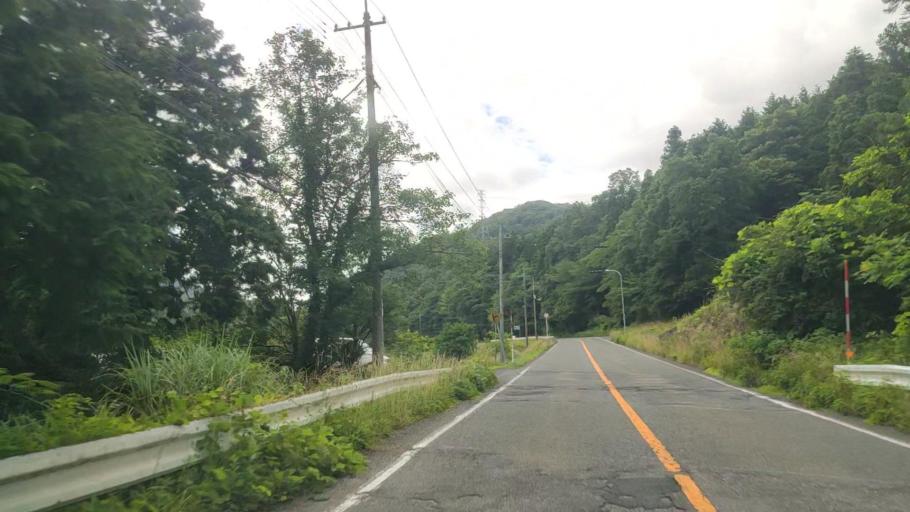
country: JP
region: Tottori
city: Yonago
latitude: 35.2892
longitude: 133.4226
